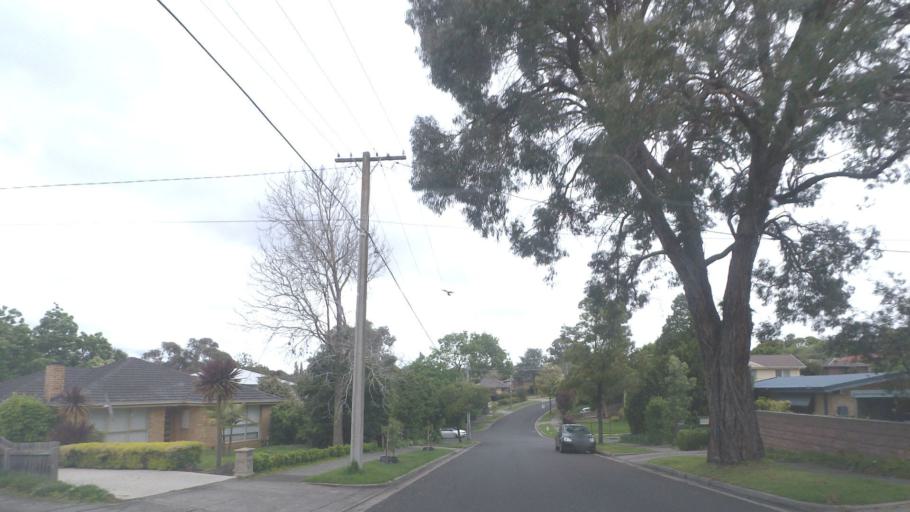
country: AU
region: Victoria
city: Mitcham
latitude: -37.8092
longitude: 145.1963
